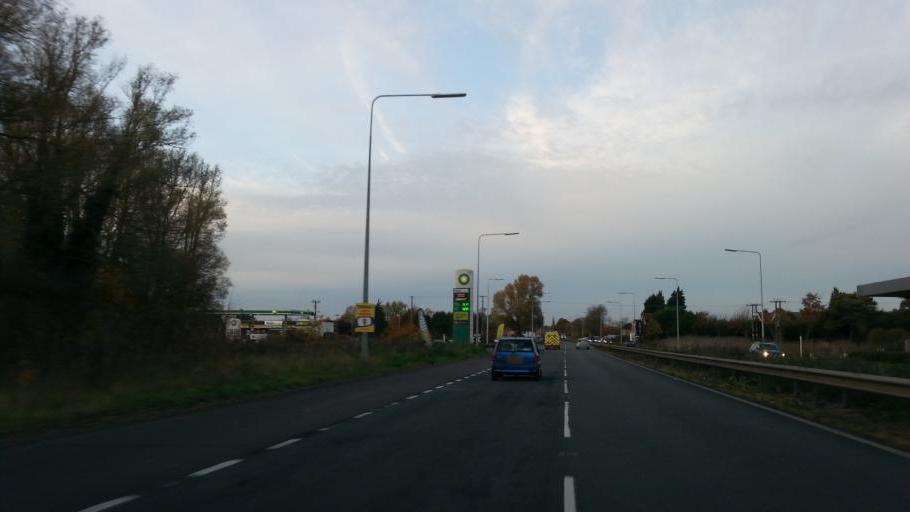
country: GB
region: England
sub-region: Central Bedfordshire
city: Astwick
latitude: 52.0277
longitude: -0.2137
